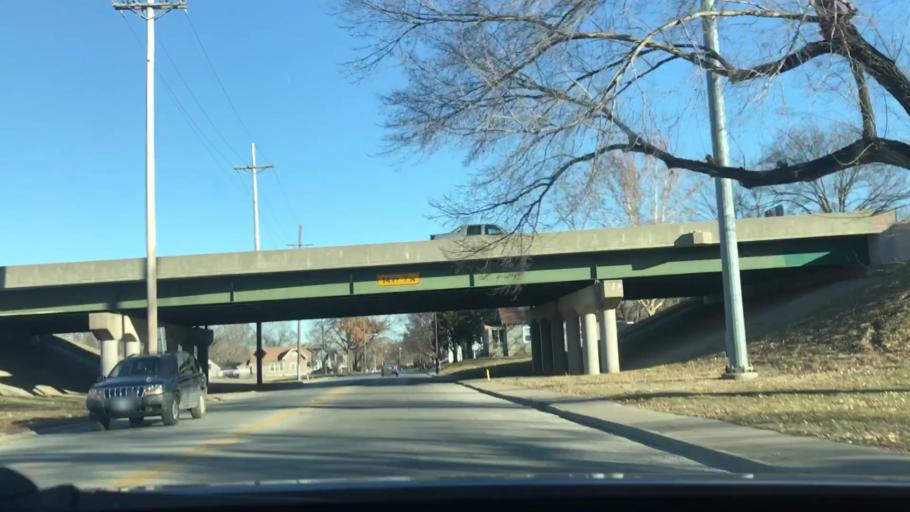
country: US
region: Kansas
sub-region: Johnson County
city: Roeland Park
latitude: 39.0729
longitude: -94.6512
